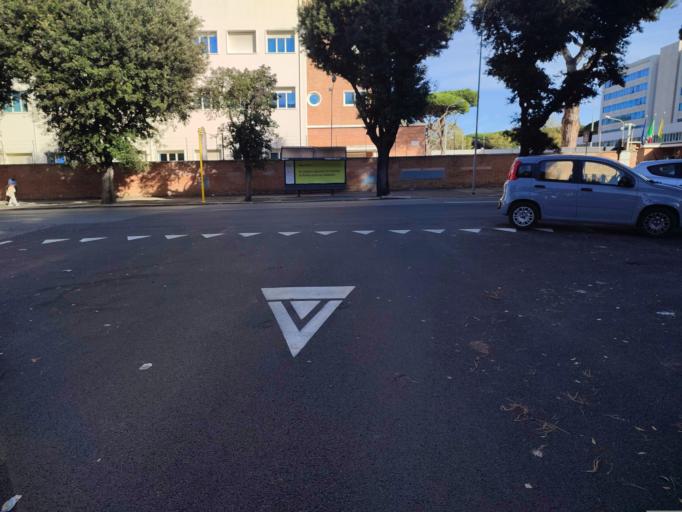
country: IT
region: Latium
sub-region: Citta metropolitana di Roma Capitale
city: Lido di Ostia
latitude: 41.7328
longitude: 12.2926
